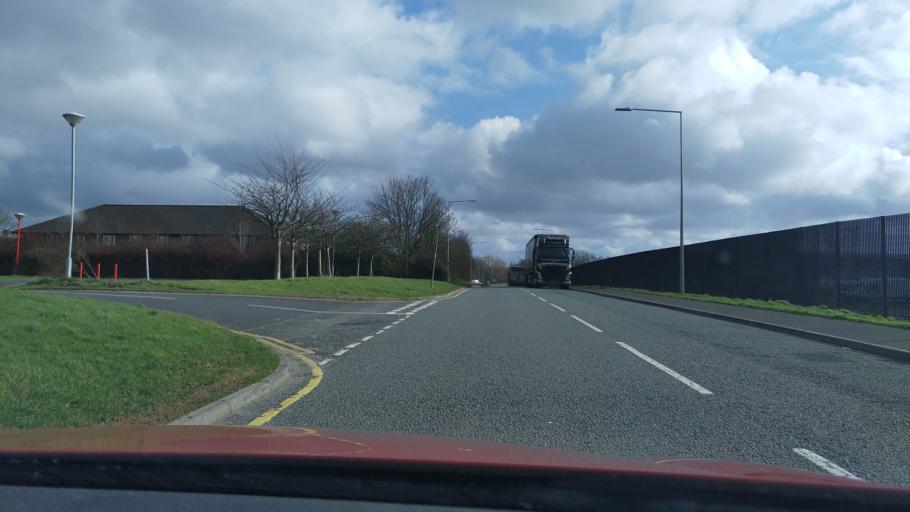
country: GB
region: England
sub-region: Lancashire
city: Goosnargh
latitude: 53.7975
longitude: -2.6918
